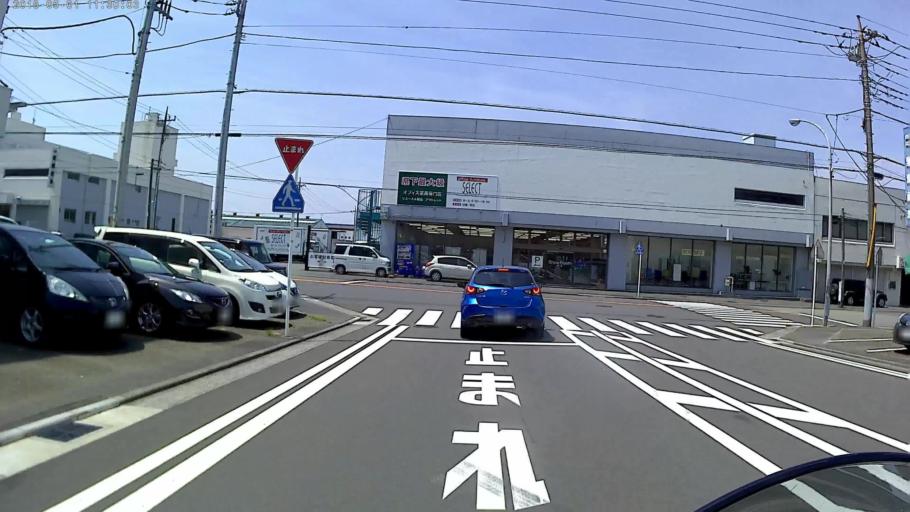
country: JP
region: Kanagawa
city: Minami-rinkan
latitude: 35.5007
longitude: 139.4864
